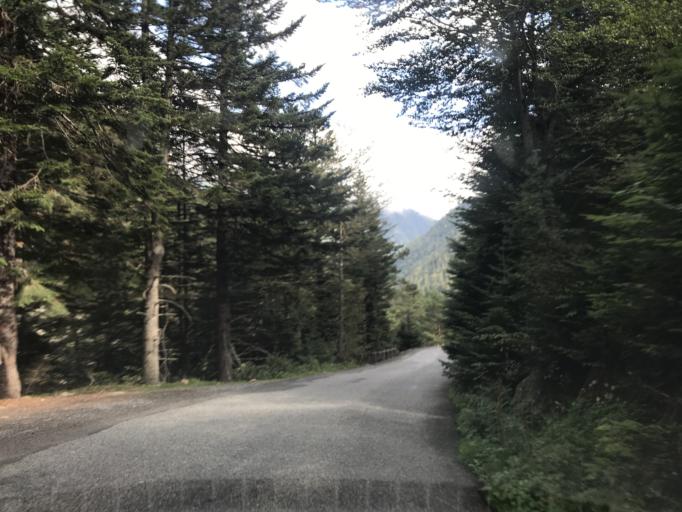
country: FR
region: Midi-Pyrenees
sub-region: Departement des Hautes-Pyrenees
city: Saint-Lary-Soulan
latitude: 42.8177
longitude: 0.1949
